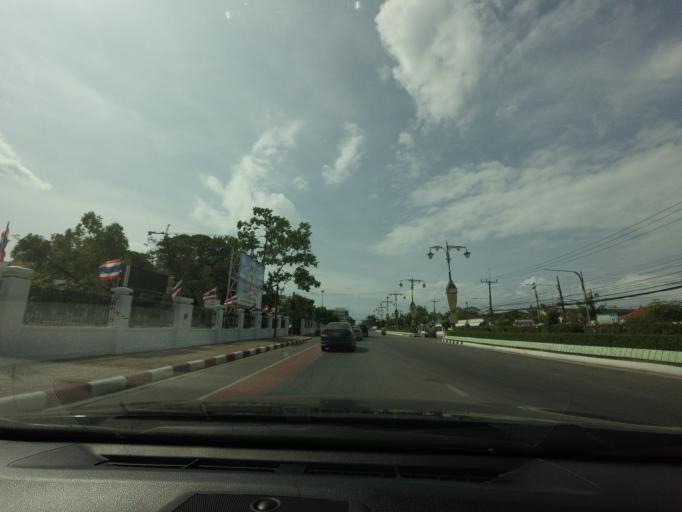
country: TH
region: Pattani
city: Pattani
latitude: 6.8680
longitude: 101.2507
